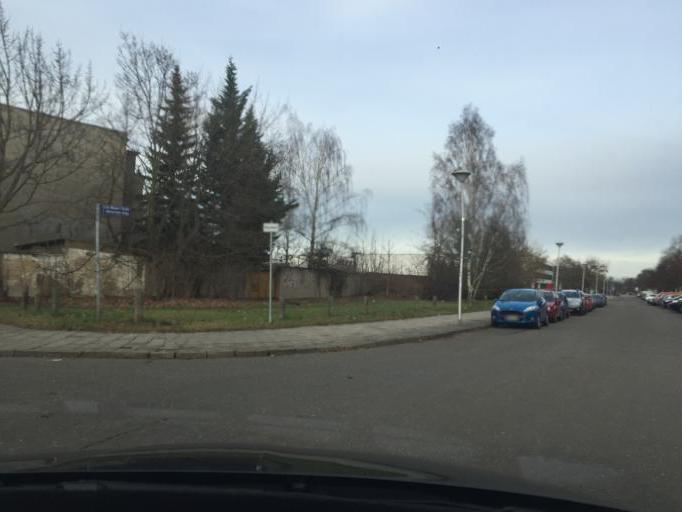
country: DE
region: Brandenburg
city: Cottbus
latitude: 51.7638
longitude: 14.3245
